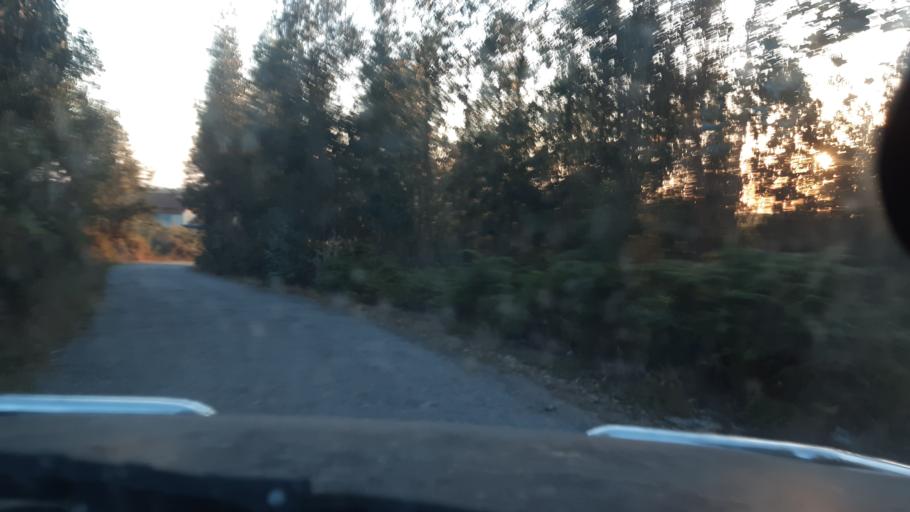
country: PT
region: Aveiro
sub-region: Agueda
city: Aguada de Cima
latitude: 40.5637
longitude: -8.3494
